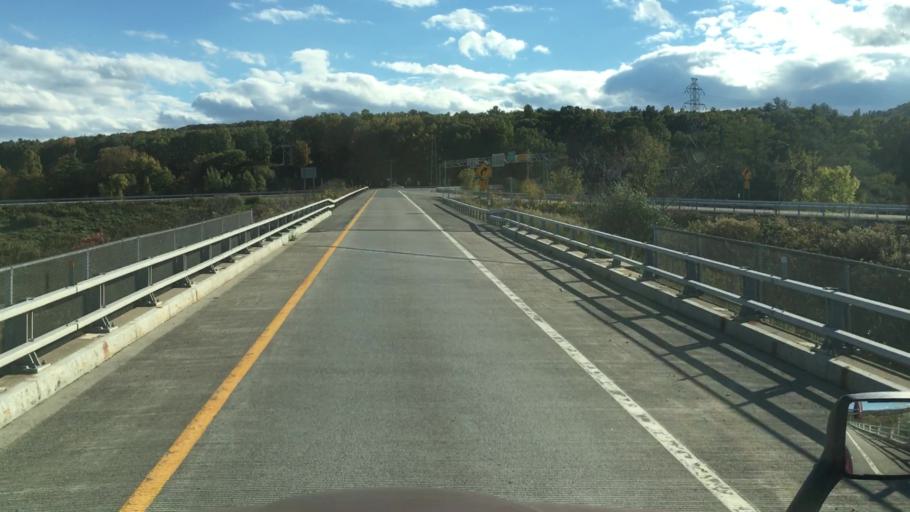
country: US
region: New York
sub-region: Schenectady County
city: Scotia
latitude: 42.8428
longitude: -74.0063
